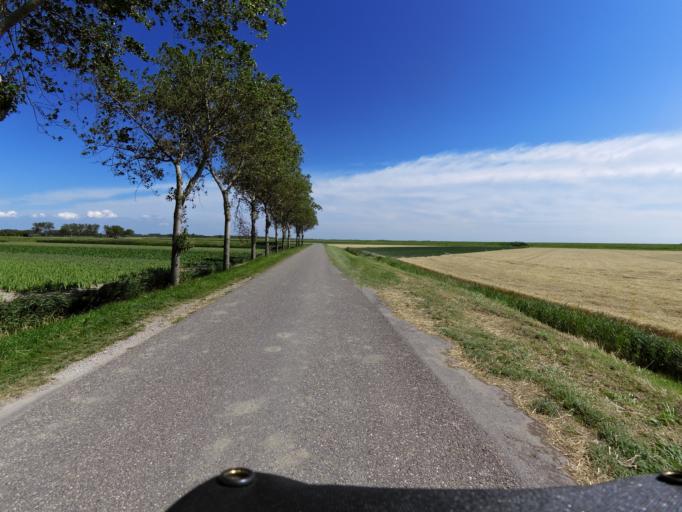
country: NL
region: South Holland
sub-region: Gemeente Goeree-Overflakkee
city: Goedereede
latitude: 51.8040
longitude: 3.9746
